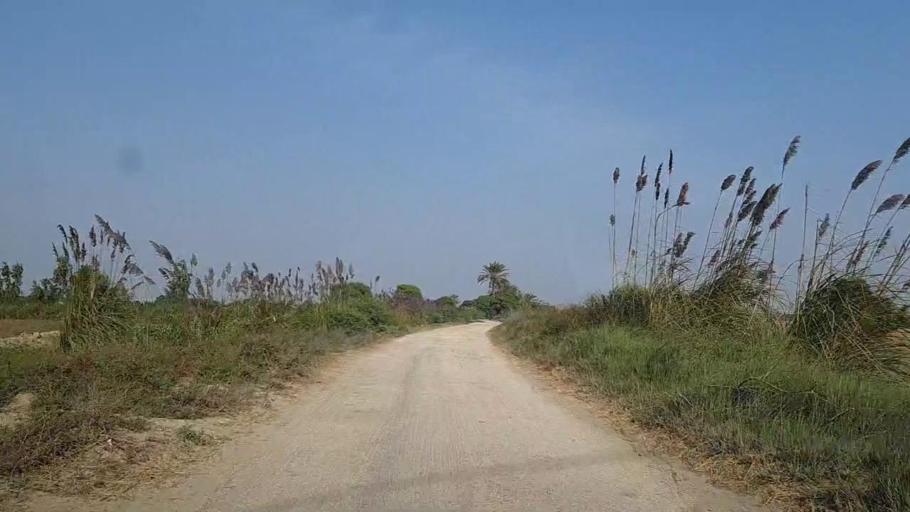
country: PK
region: Sindh
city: Mirpur Sakro
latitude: 24.5953
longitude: 67.5815
